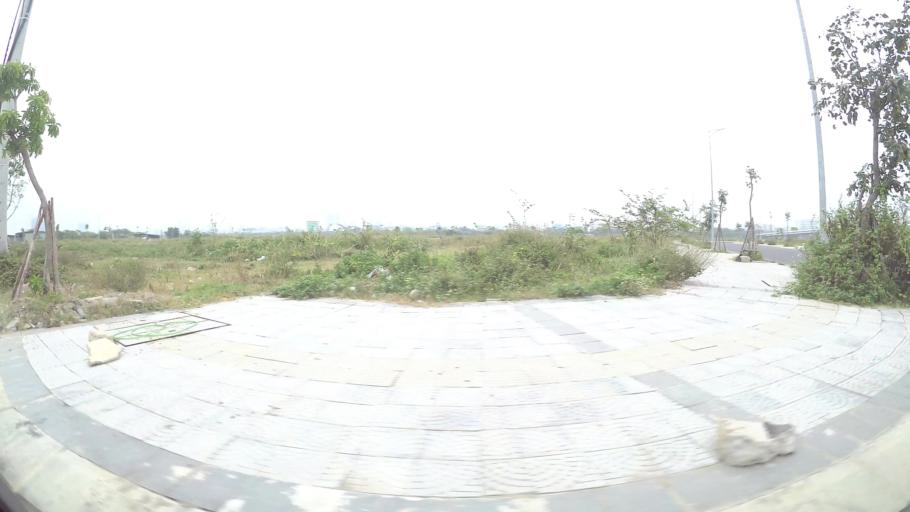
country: VN
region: Da Nang
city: Son Tra
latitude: 16.0364
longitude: 108.2330
